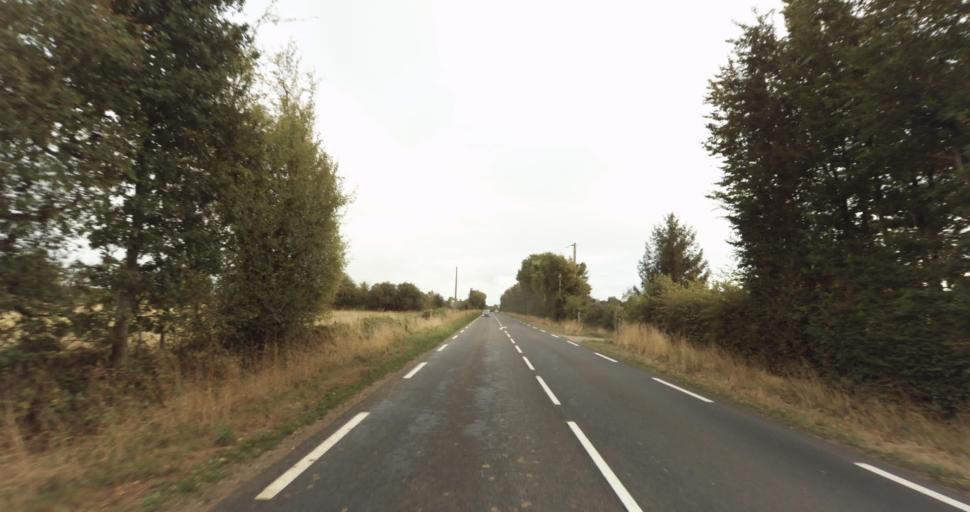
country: FR
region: Lower Normandy
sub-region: Departement de l'Orne
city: Vimoutiers
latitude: 48.8808
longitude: 0.2561
